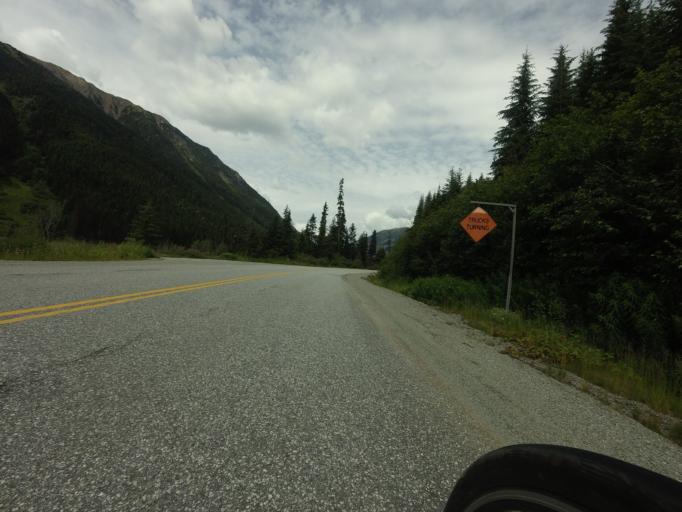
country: CA
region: British Columbia
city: Lillooet
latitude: 50.4116
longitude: -122.2900
